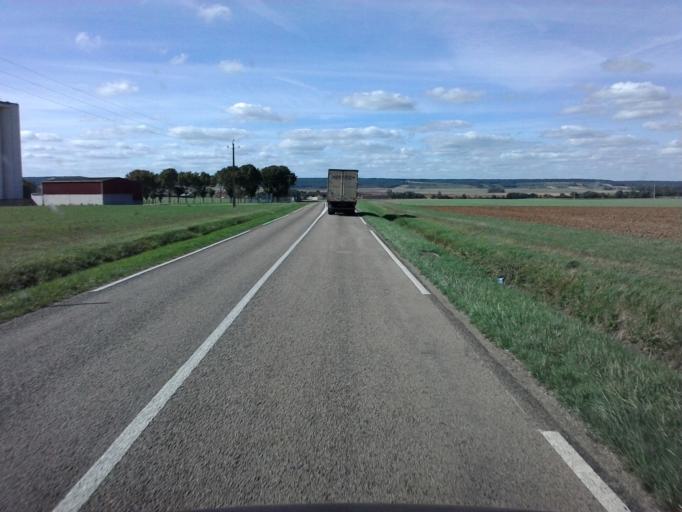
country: FR
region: Bourgogne
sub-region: Departement de la Cote-d'Or
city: Chatillon-sur-Seine
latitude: 47.9096
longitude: 4.6814
